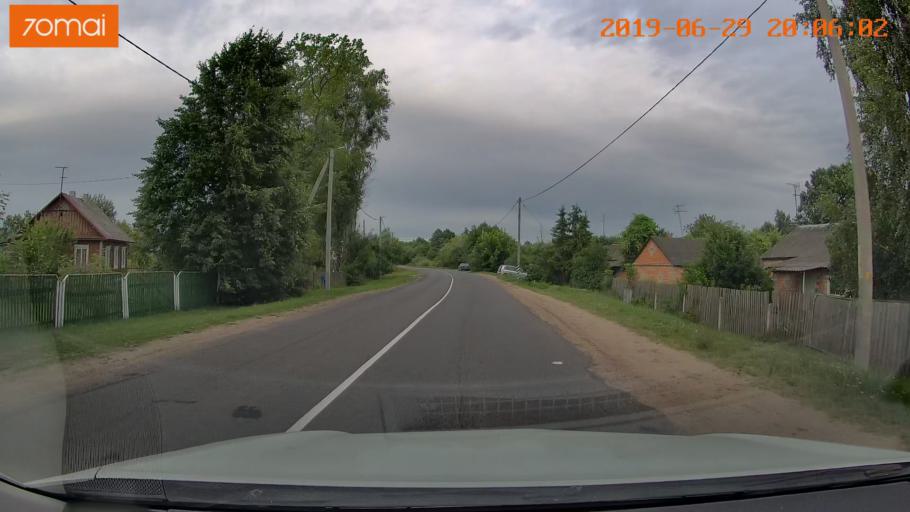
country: BY
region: Brest
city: Lahishyn
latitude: 52.3383
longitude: 26.0051
